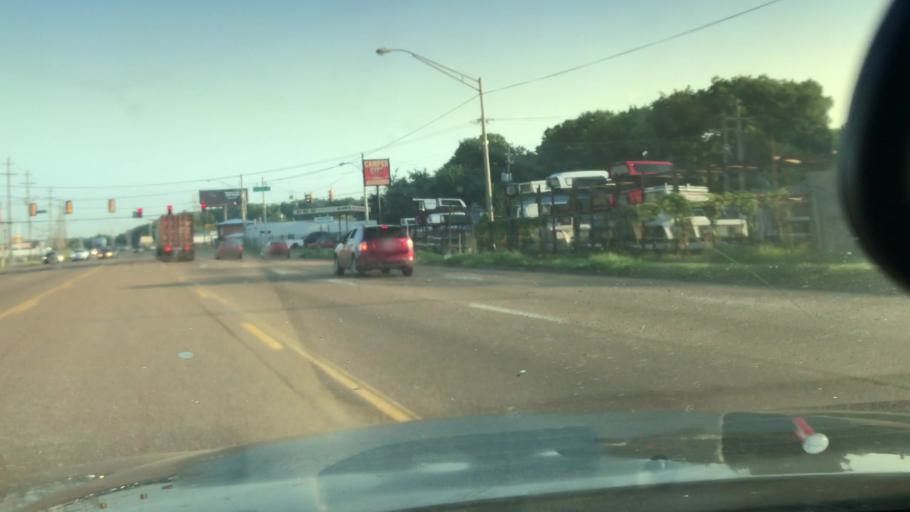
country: US
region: Mississippi
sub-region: De Soto County
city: Southaven
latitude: 35.0718
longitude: -89.9467
